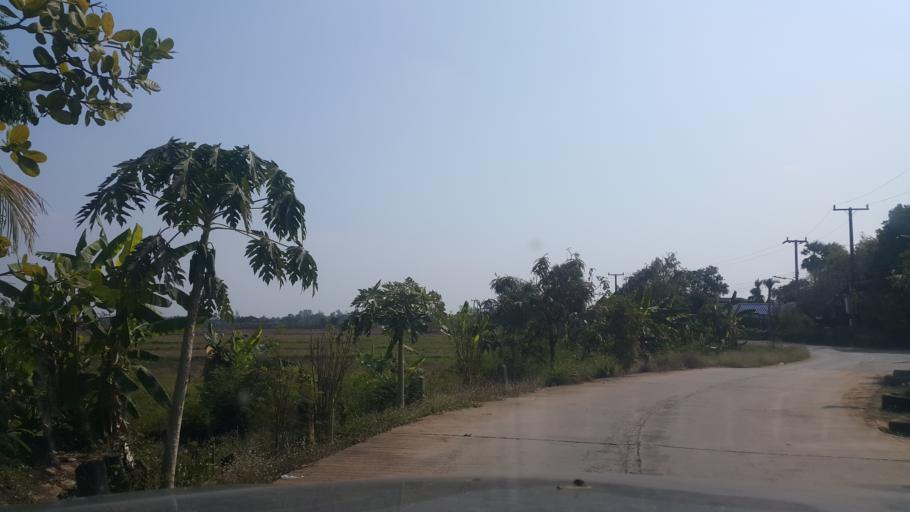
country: TH
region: Nakhon Ratchasima
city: Chok Chai
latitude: 14.7006
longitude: 102.1168
